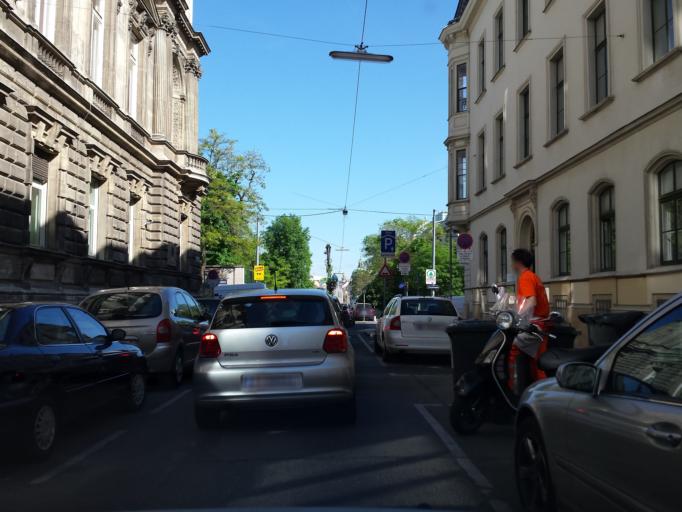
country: AT
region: Vienna
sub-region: Wien Stadt
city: Vienna
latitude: 48.1916
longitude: 16.3750
